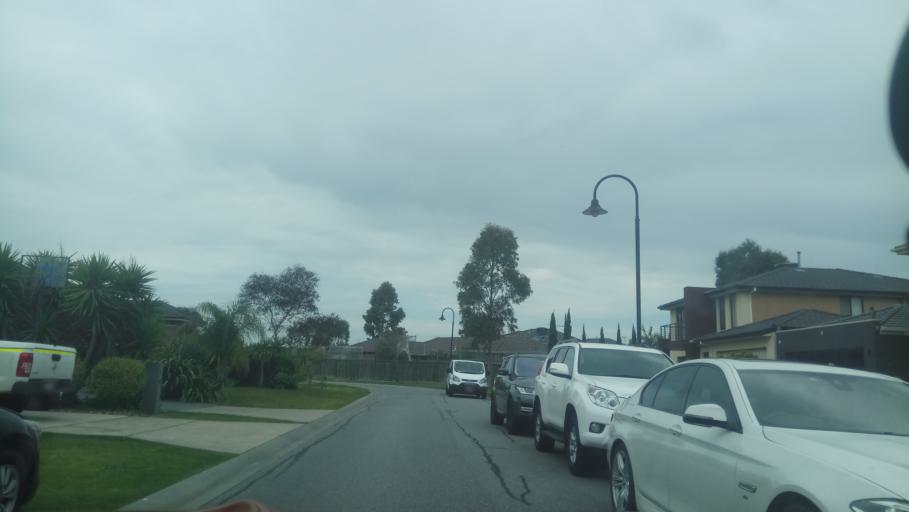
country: AU
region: Victoria
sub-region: Kingston
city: Waterways
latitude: -38.0117
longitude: 145.1343
